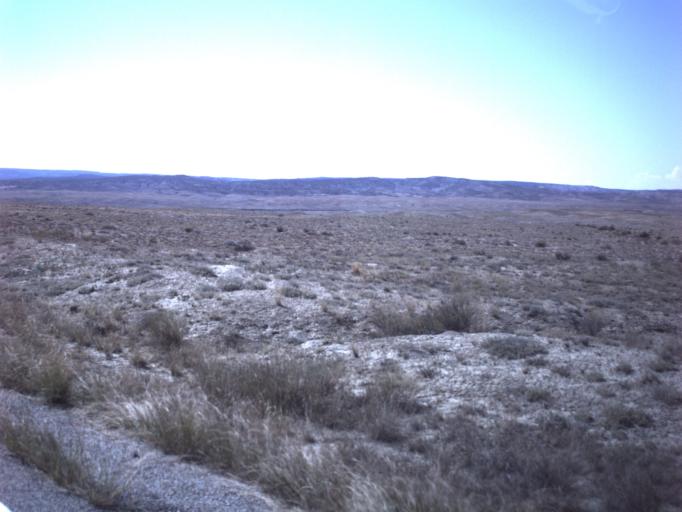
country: US
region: Utah
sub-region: Grand County
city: Moab
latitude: 38.9087
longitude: -109.3251
